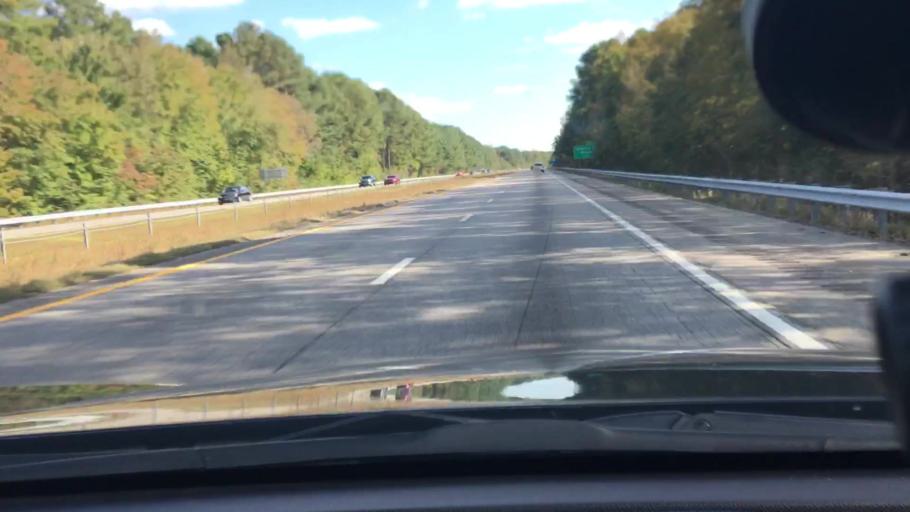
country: US
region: North Carolina
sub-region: Wilson County
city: Lucama
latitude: 35.7055
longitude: -77.9902
